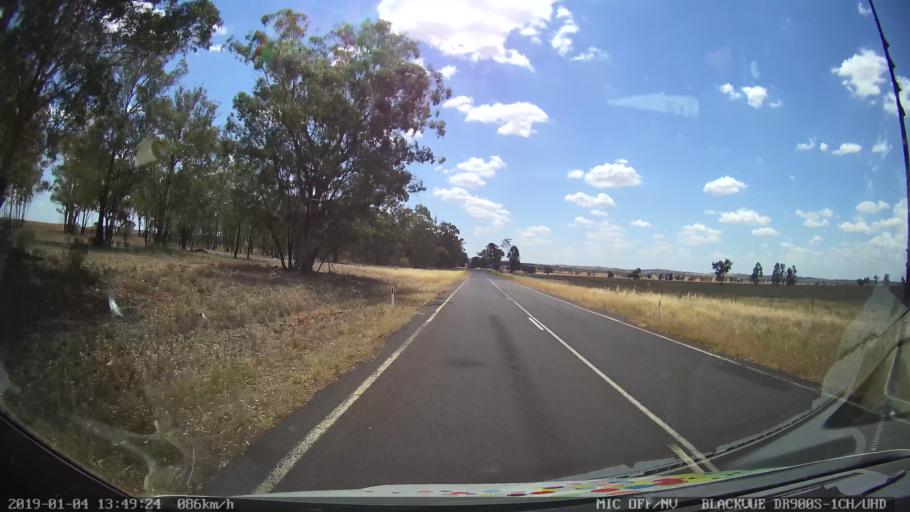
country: AU
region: New South Wales
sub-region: Dubbo Municipality
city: Dubbo
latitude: -32.4325
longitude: 148.5793
